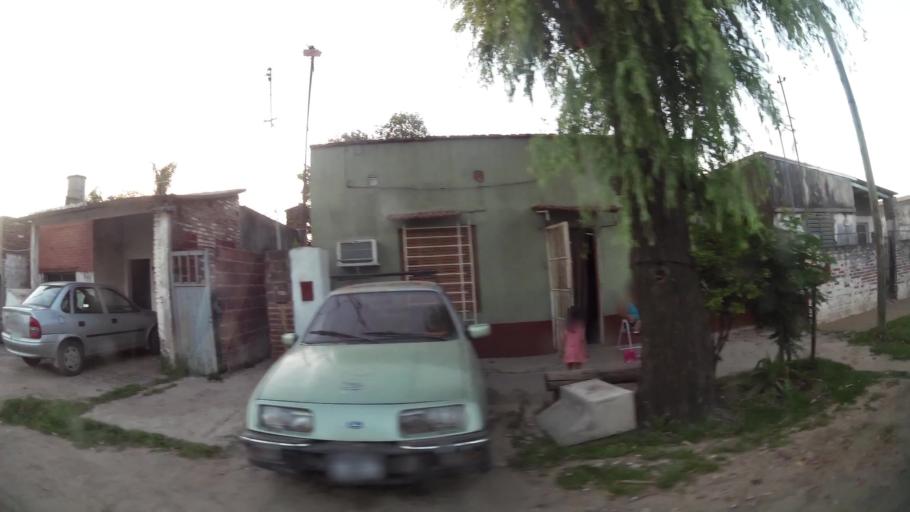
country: AR
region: Santa Fe
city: Santa Fe de la Vera Cruz
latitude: -31.5957
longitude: -60.6967
